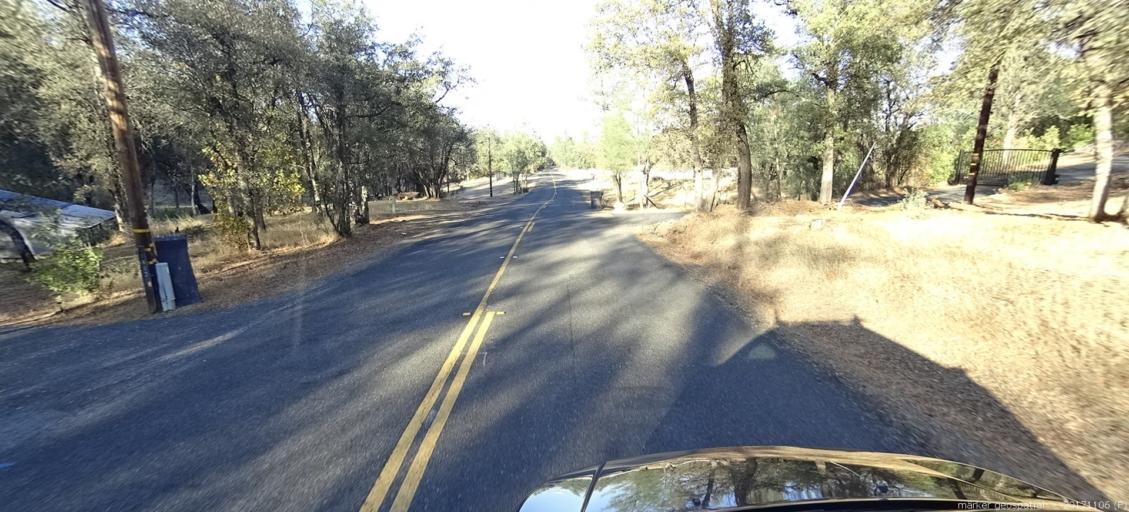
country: US
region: California
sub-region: Shasta County
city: Shasta
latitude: 40.5672
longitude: -122.4686
